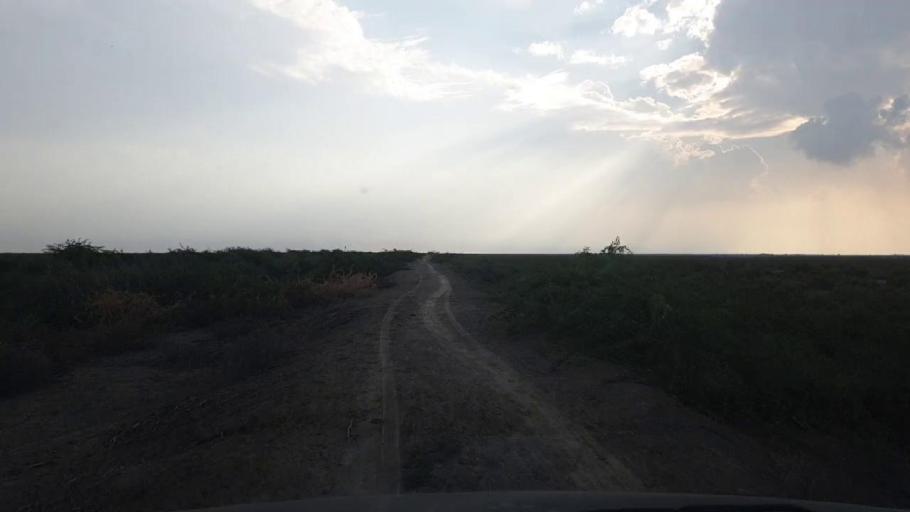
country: PK
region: Sindh
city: Badin
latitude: 24.4570
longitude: 68.6872
